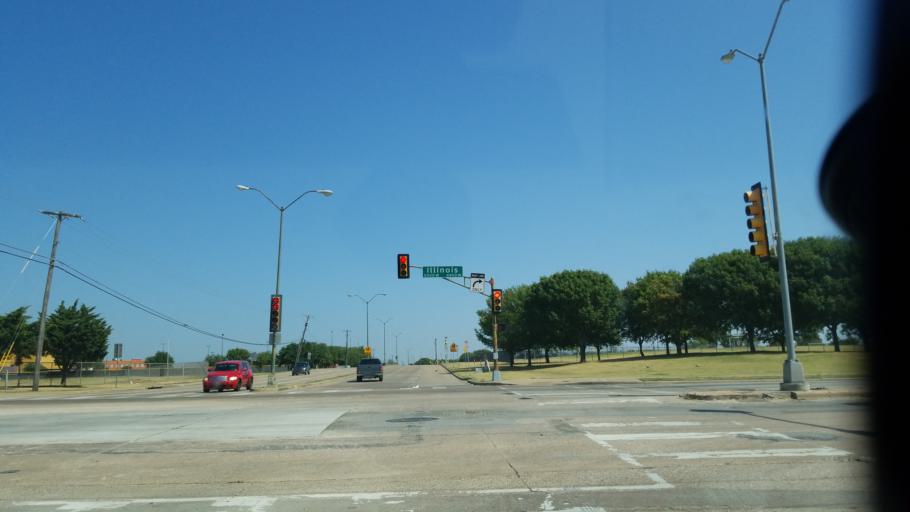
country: US
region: Texas
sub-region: Dallas County
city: Cockrell Hill
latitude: 32.7203
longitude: -96.9086
